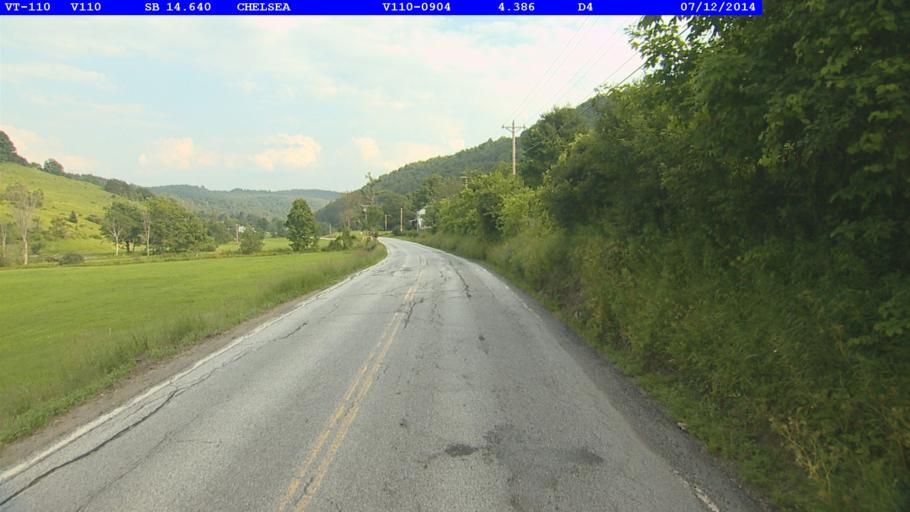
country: US
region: Vermont
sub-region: Orange County
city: Chelsea
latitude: 44.0060
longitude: -72.4594
